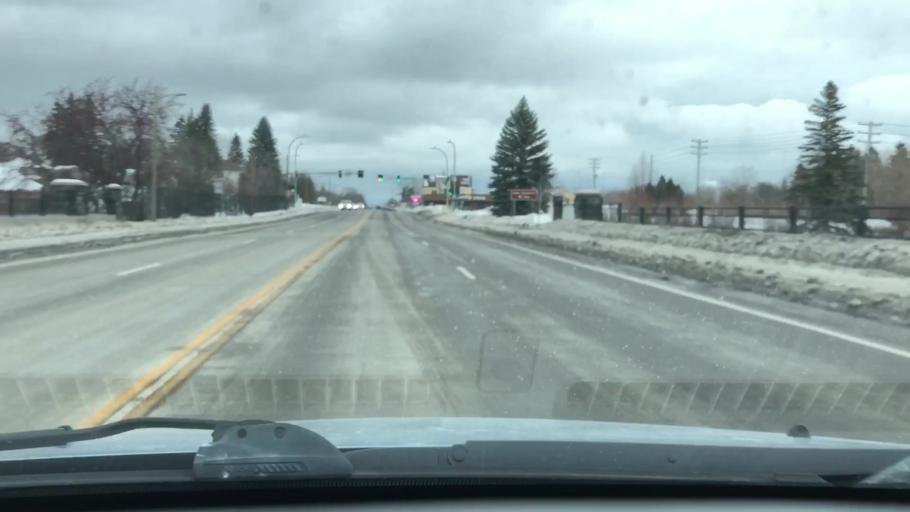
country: US
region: Minnesota
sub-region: Saint Louis County
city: Proctor
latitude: 46.7245
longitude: -92.1897
